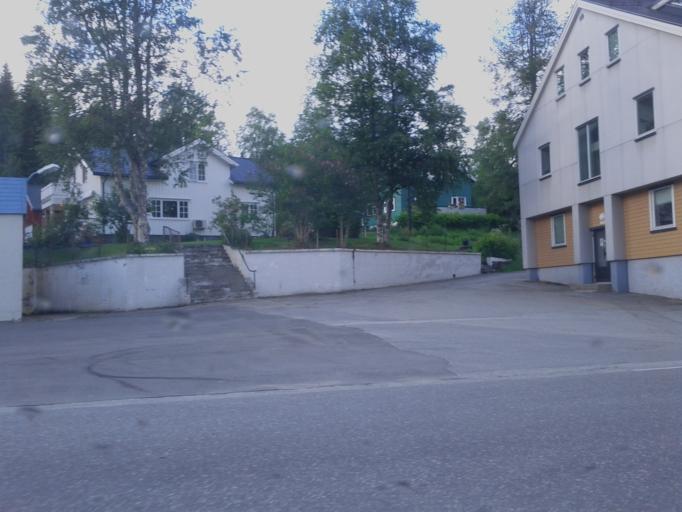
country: NO
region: Nordland
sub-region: Hattfjelldal
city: Hattfjelldal
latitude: 65.5974
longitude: 13.9889
